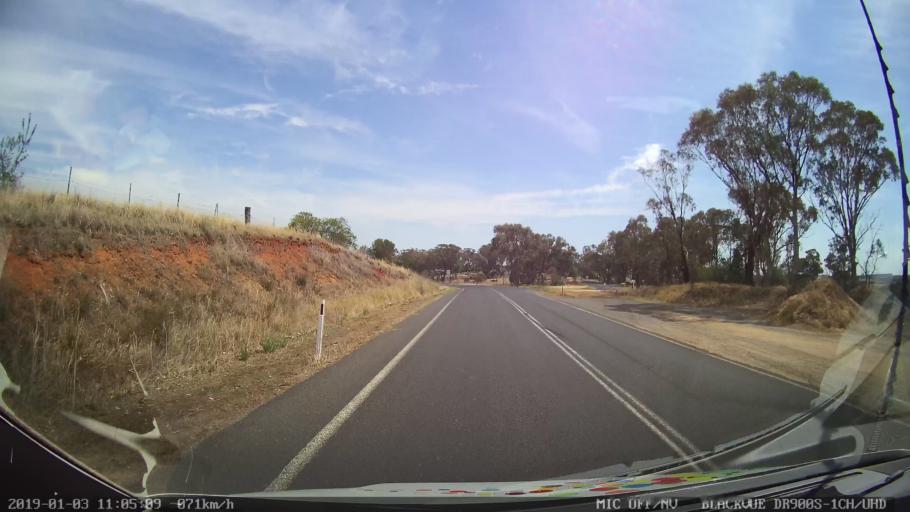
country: AU
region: New South Wales
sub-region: Young
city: Young
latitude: -34.2746
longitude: 148.2862
